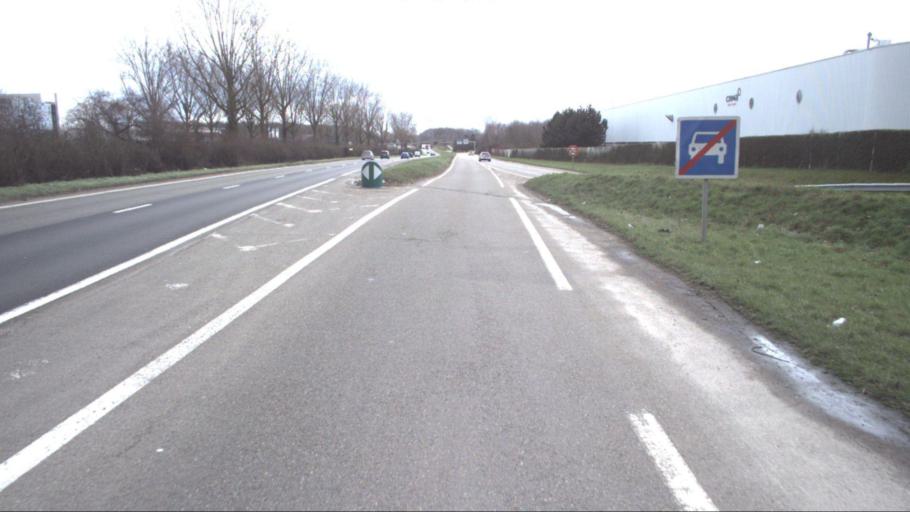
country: FR
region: Ile-de-France
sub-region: Departement des Yvelines
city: Les Clayes-sous-Bois
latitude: 48.8001
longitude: 1.9799
